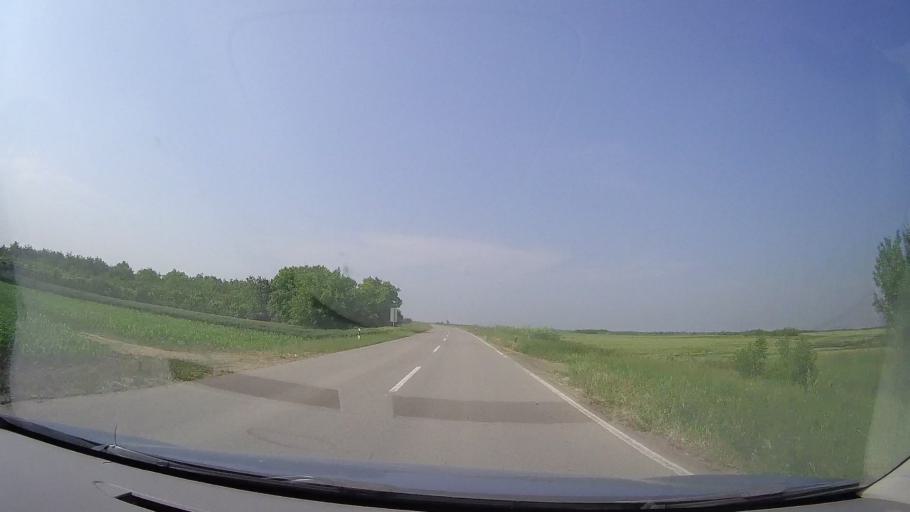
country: RS
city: Jasa Tomic
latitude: 45.4315
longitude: 20.8409
